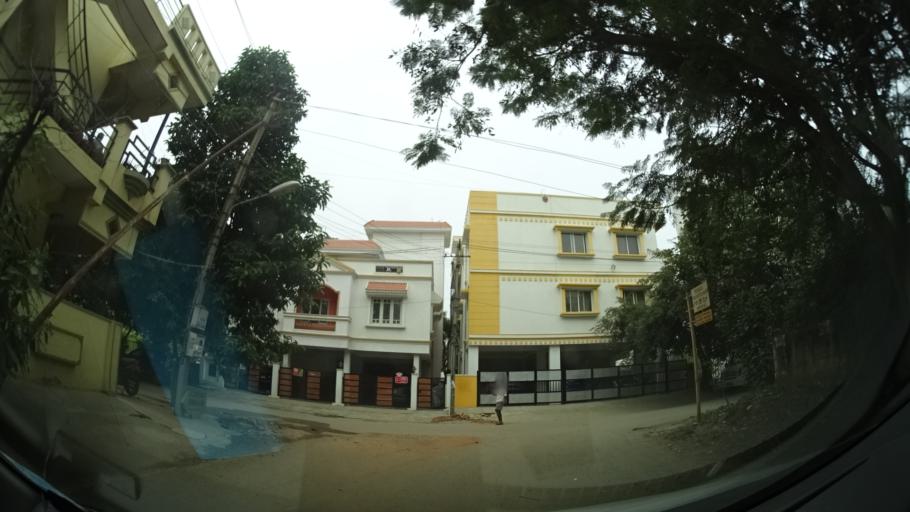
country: IN
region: Karnataka
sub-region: Bangalore Urban
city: Bangalore
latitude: 12.9587
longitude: 77.7179
